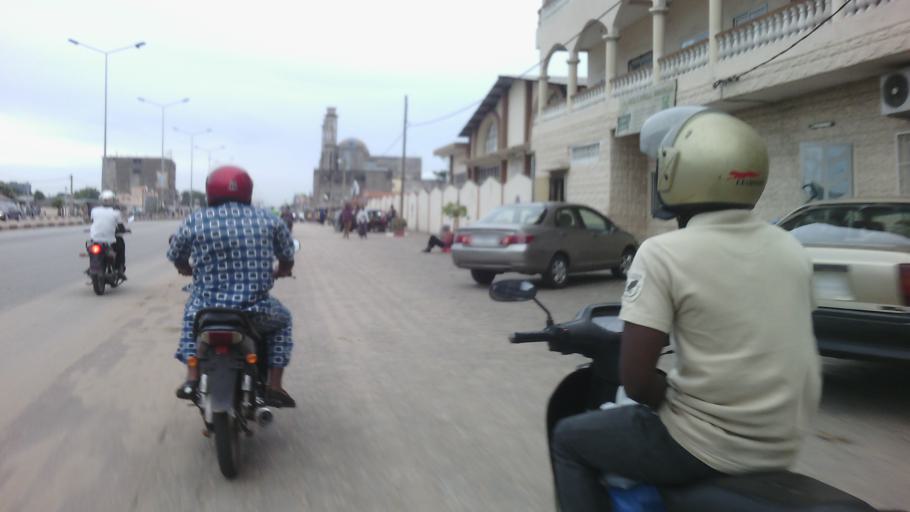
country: BJ
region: Littoral
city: Cotonou
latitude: 6.3665
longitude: 2.4153
